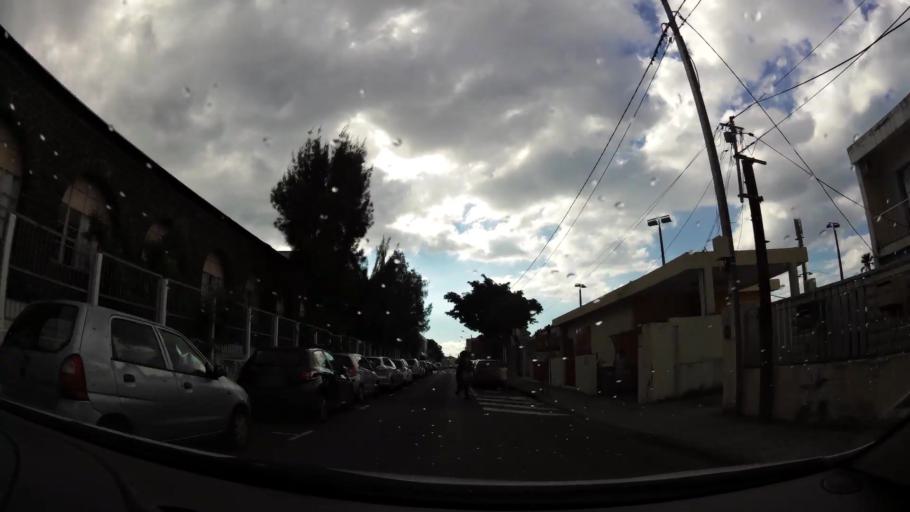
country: RE
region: Reunion
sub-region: Reunion
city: Saint-Denis
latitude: -20.8843
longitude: 55.4549
